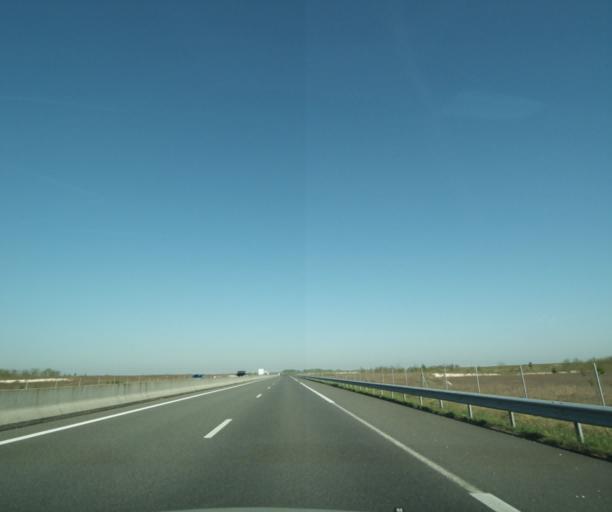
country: FR
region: Centre
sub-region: Departement du Loiret
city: Pannes
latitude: 48.0722
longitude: 2.6412
